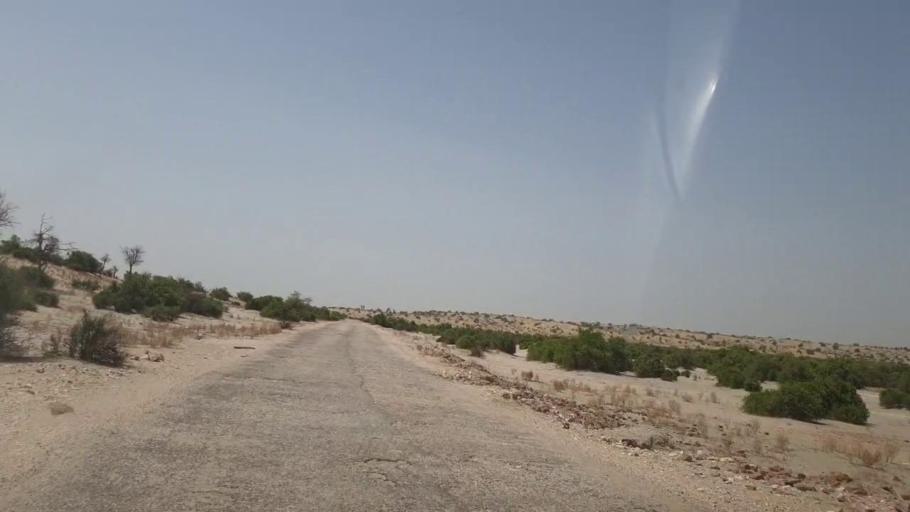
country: PK
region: Sindh
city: Khanpur
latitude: 27.3564
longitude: 69.3180
